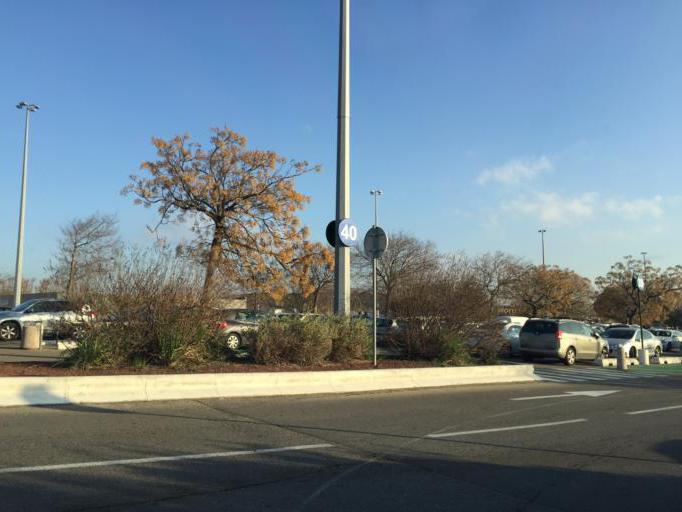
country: FR
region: Provence-Alpes-Cote d'Azur
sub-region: Departement du Vaucluse
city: Vedene
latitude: 43.9849
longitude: 4.8826
